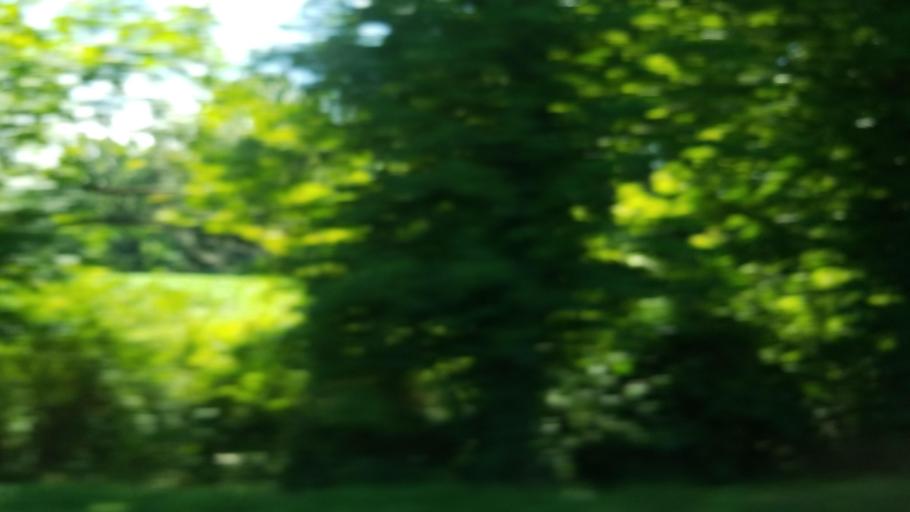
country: US
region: Illinois
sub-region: Williamson County
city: Johnston City
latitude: 37.7894
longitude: -88.9229
